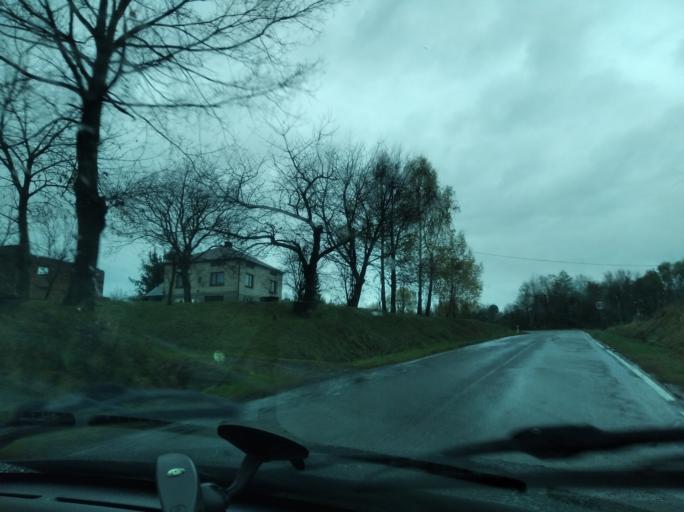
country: PL
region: Subcarpathian Voivodeship
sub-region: Powiat lancucki
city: Handzlowka
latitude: 49.9842
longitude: 22.1921
